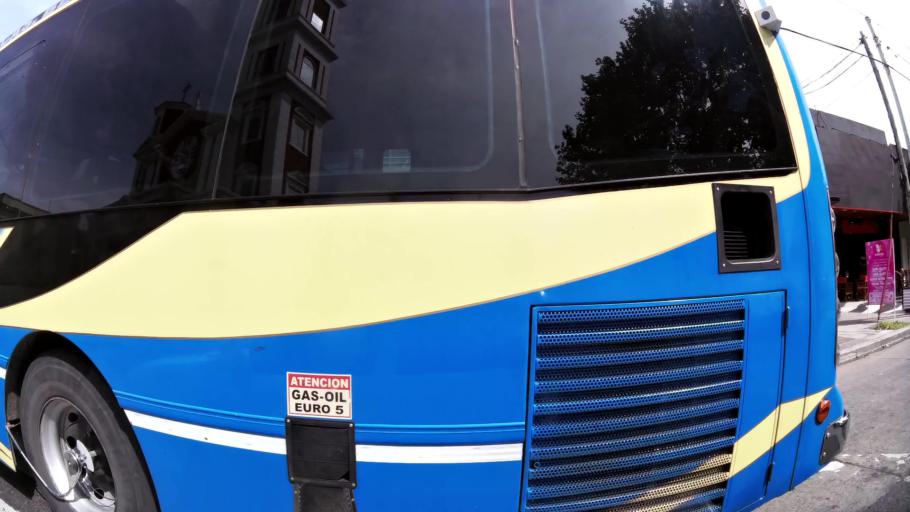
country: AR
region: Buenos Aires F.D.
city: Villa Lugano
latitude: -34.6503
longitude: -58.5118
